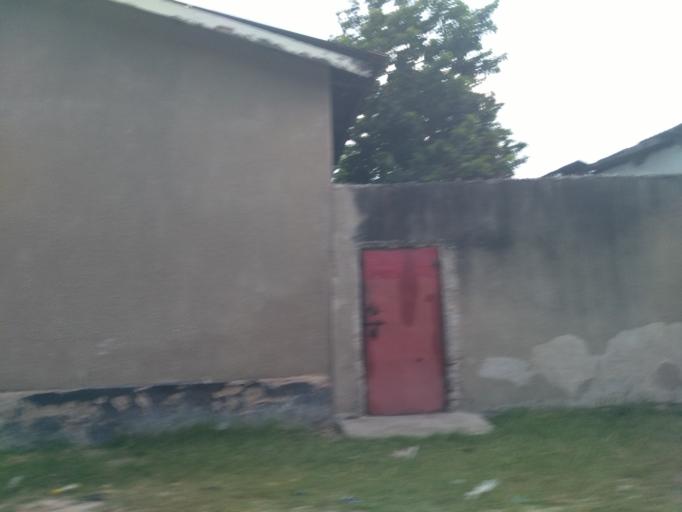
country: TZ
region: Dar es Salaam
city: Dar es Salaam
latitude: -6.8239
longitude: 39.3064
